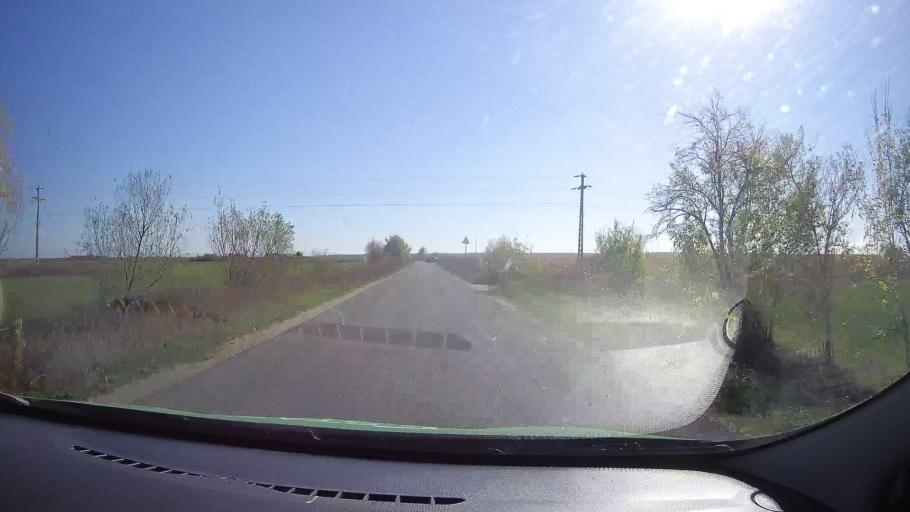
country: RO
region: Satu Mare
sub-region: Comuna Doba
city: Doba
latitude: 47.7398
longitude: 22.7174
